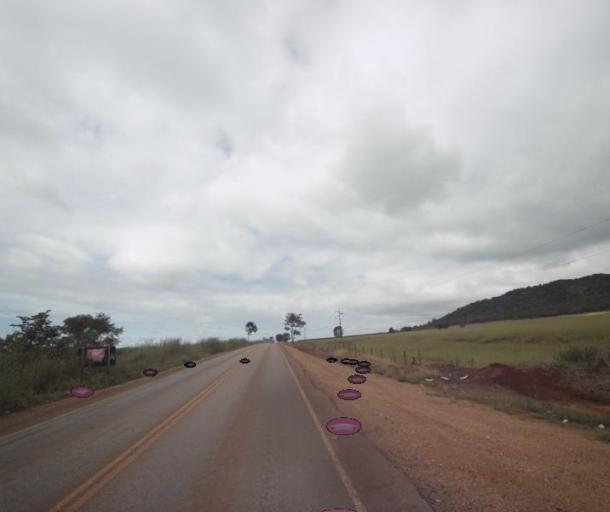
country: BR
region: Goias
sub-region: Barro Alto
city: Barro Alto
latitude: -15.0248
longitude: -48.8969
